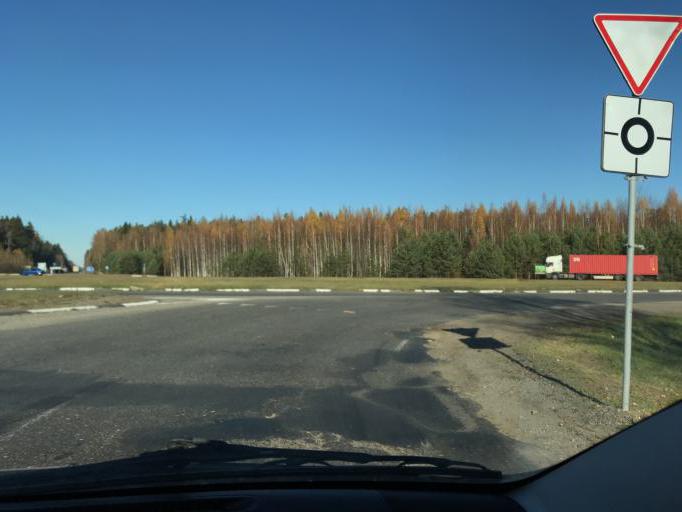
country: BY
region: Vitebsk
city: Polatsk
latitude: 55.5390
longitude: 28.7150
